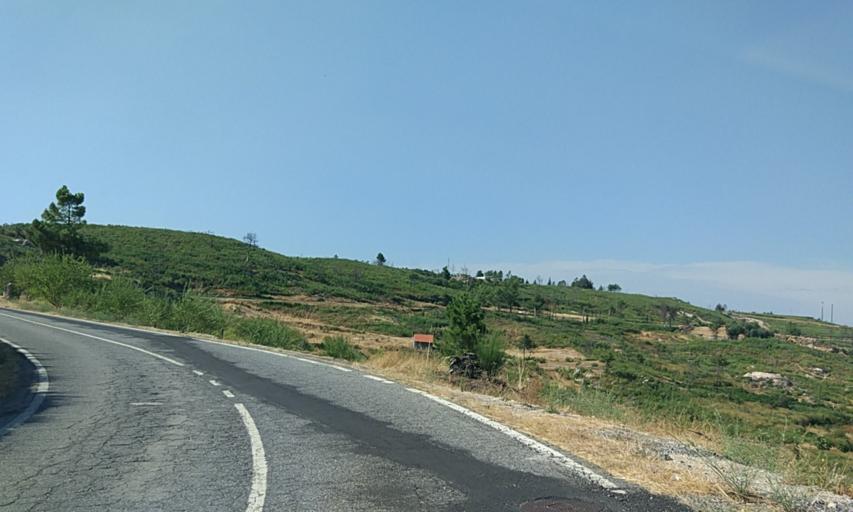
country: PT
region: Vila Real
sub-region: Sabrosa
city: Sabrosa
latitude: 41.3008
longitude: -7.4748
